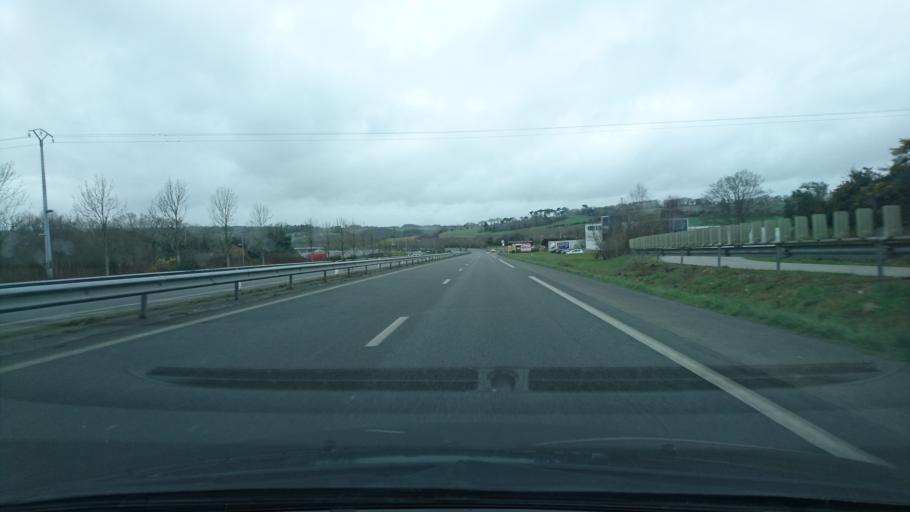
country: FR
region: Brittany
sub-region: Departement du Finistere
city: Morlaix
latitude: 48.5784
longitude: -3.8610
